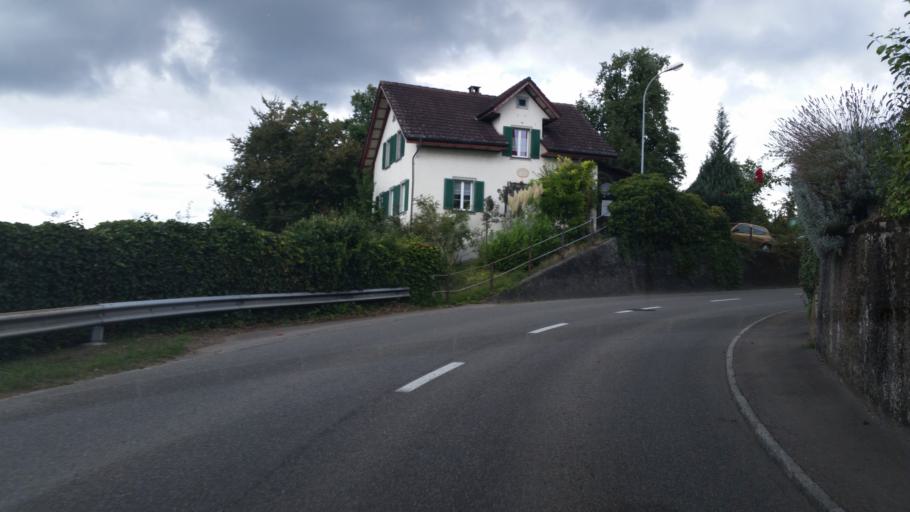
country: CH
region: Aargau
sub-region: Bezirk Bremgarten
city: Oberlunkhofen
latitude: 47.3129
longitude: 8.3919
